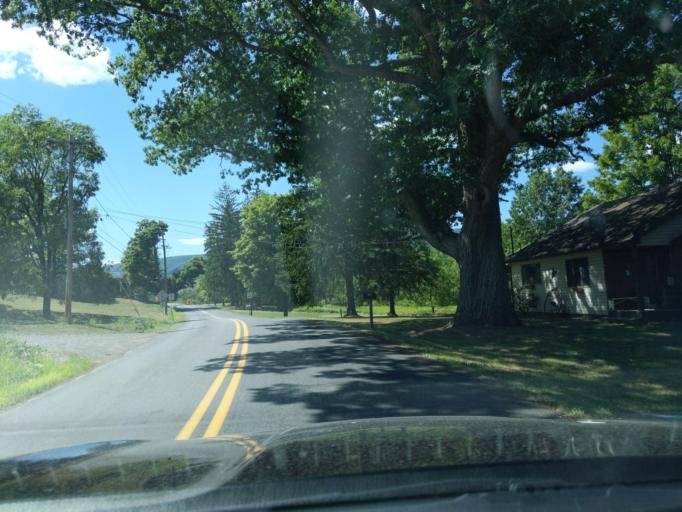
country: US
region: Pennsylvania
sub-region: Blair County
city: Williamsburg
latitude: 40.4772
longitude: -78.2876
